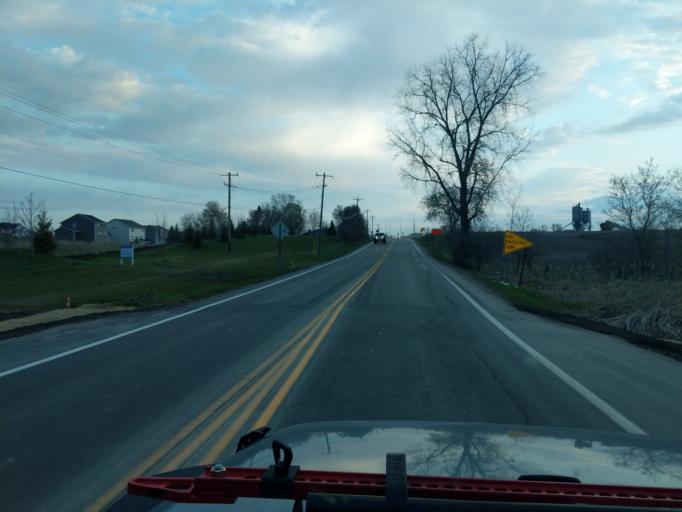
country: US
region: Minnesota
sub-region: Hennepin County
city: Rogers
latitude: 45.1596
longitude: -93.5217
